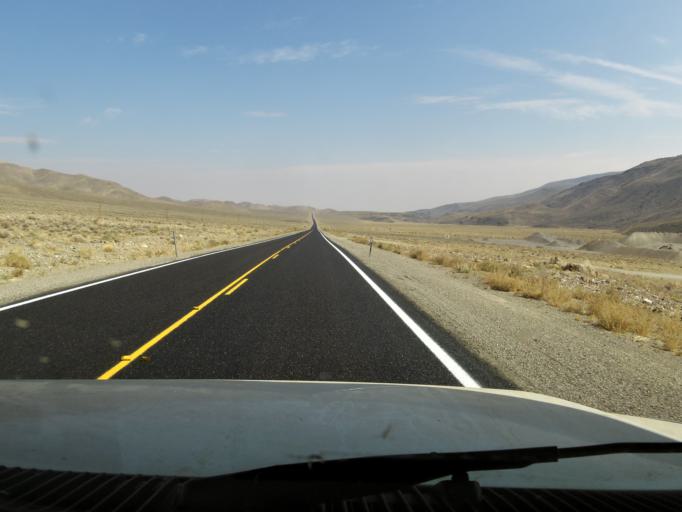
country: US
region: California
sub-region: Inyo County
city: Dixon Lane-Meadow Creek
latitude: 38.0028
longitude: -118.1669
